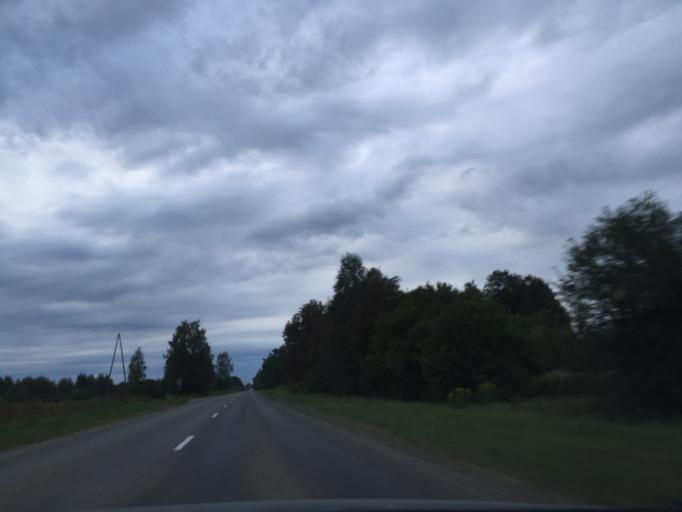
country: LV
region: Vecumnieki
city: Vecumnieki
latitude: 56.5109
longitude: 24.5630
